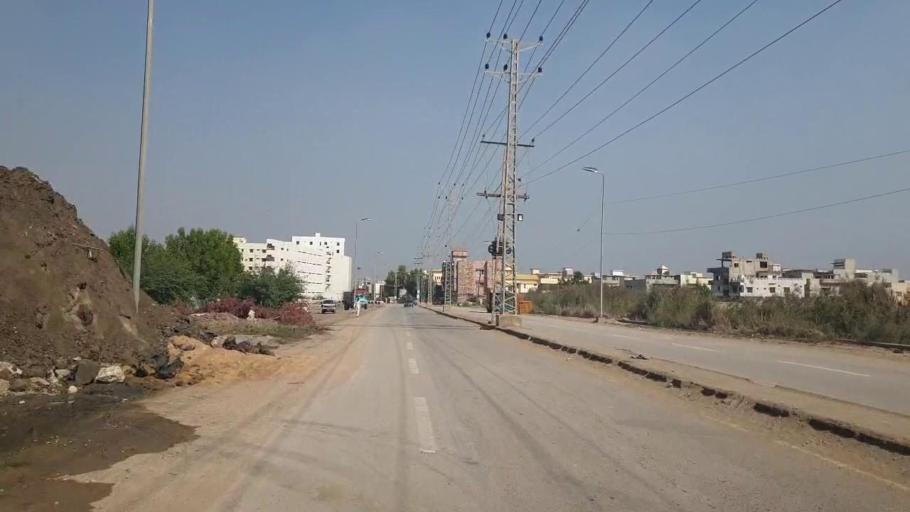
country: PK
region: Sindh
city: Hyderabad
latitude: 25.4208
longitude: 68.3530
